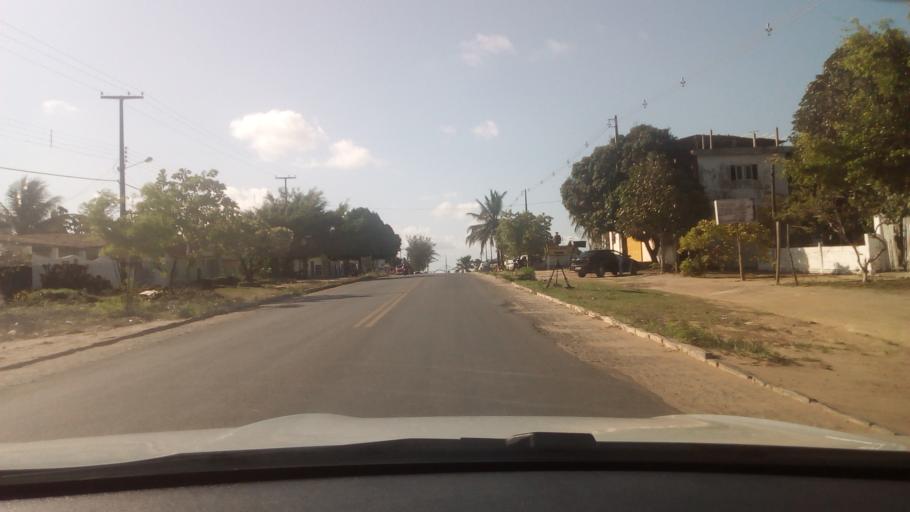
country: BR
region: Paraiba
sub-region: Conde
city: Conde
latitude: -7.2747
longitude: -34.8073
